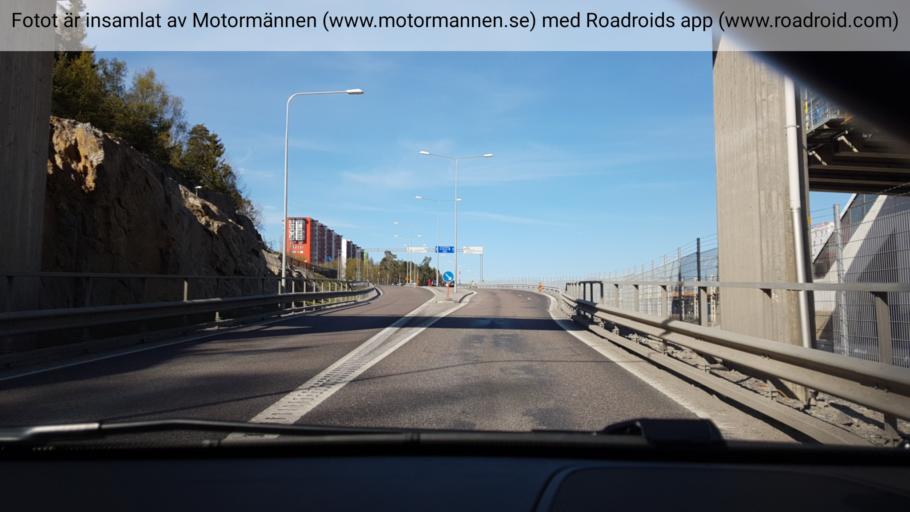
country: SE
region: Stockholm
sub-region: Huddinge Kommun
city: Huddinge
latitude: 59.2180
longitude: 17.9447
